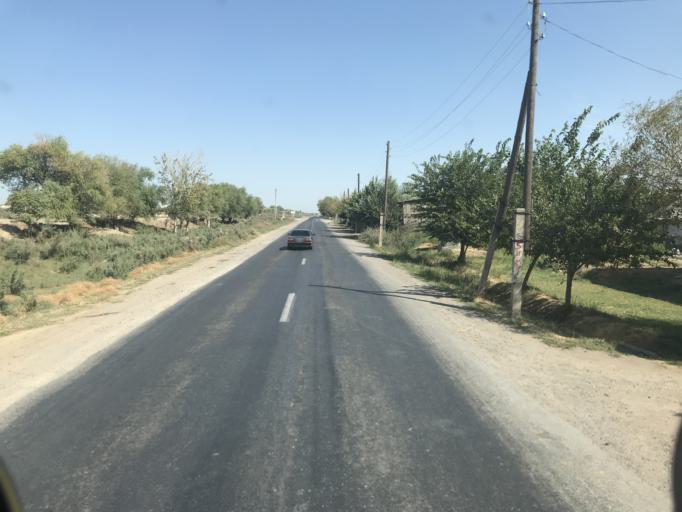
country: KZ
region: Ongtustik Qazaqstan
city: Ilyich
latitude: 40.7670
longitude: 68.5372
